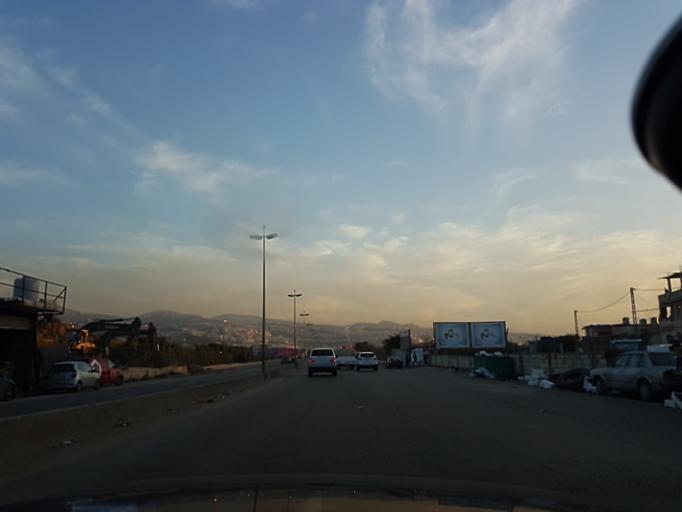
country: LB
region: Mont-Liban
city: Baabda
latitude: 33.8289
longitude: 35.4843
